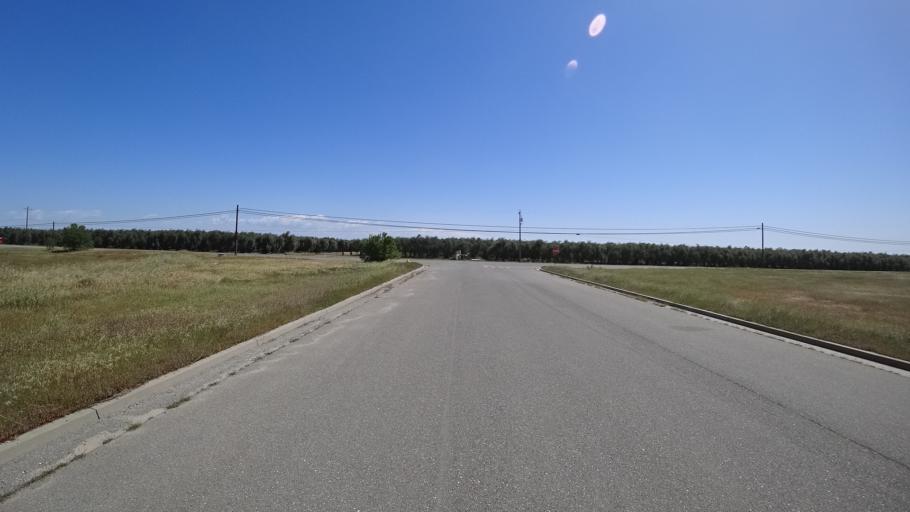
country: US
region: California
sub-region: Glenn County
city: Orland
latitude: 39.7145
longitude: -122.1418
